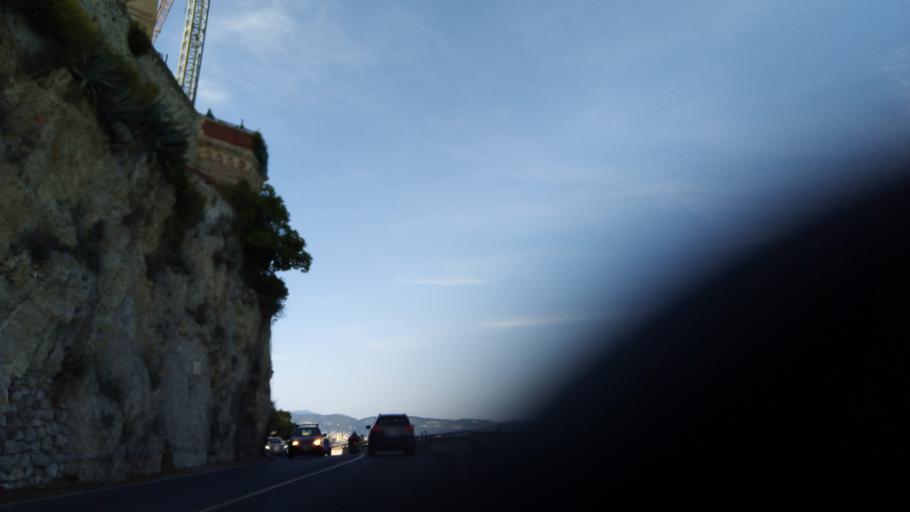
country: IT
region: Liguria
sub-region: Provincia di Savona
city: Borghetto Santo Spirito
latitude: 44.1035
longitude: 8.2384
